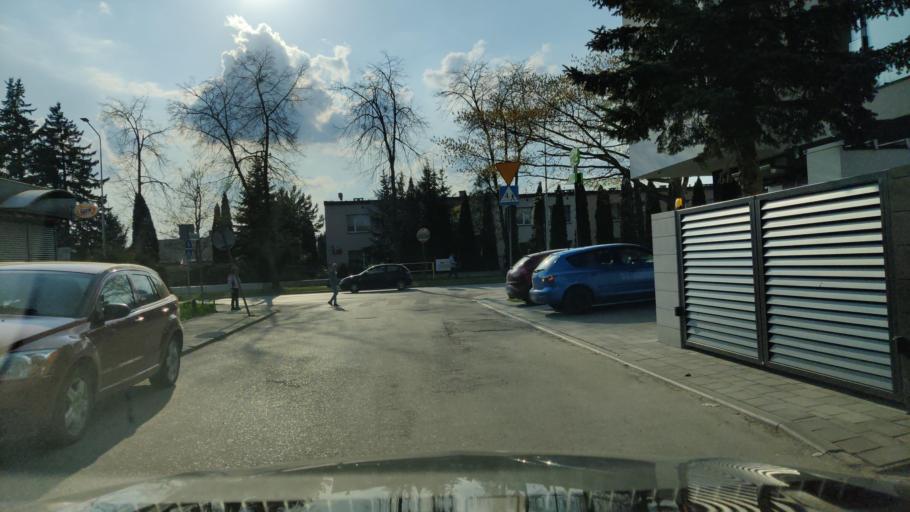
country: PL
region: Masovian Voivodeship
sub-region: Powiat pultuski
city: Pultusk
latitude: 52.7057
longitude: 21.0769
